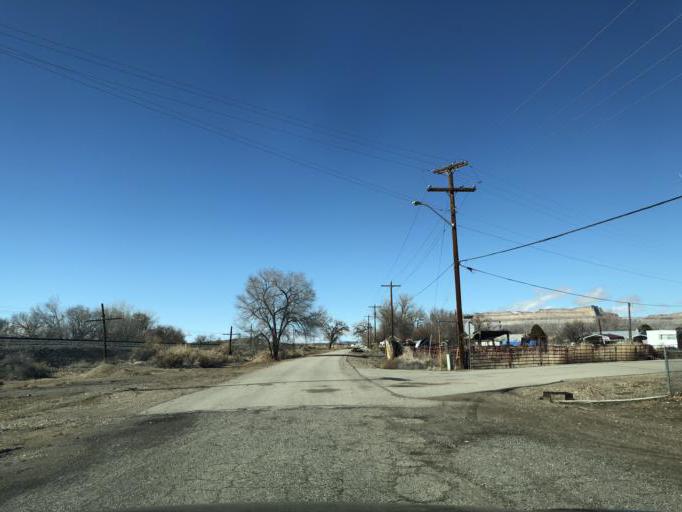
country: US
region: Utah
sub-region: Carbon County
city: East Carbon City
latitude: 38.9872
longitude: -110.1573
